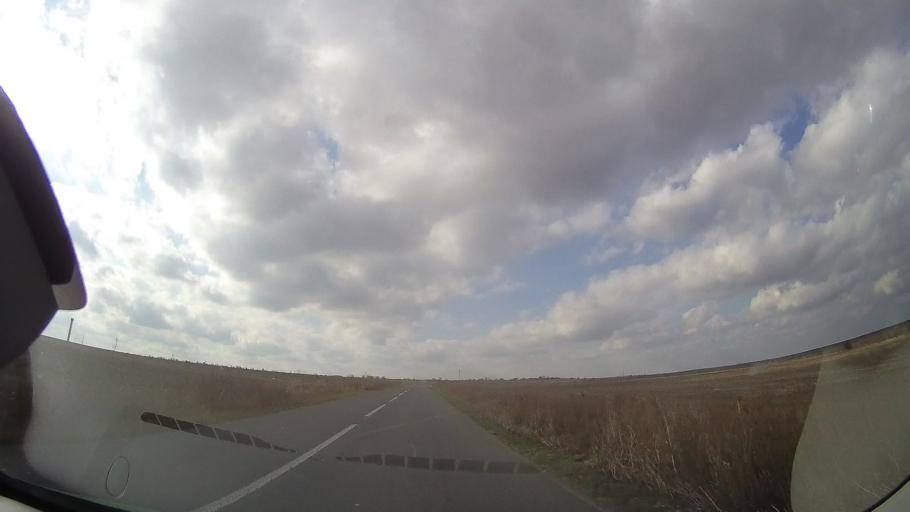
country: RO
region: Constanta
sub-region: Comuna Douazeci si Trei August
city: Dulcesti
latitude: 43.8989
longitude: 28.5277
